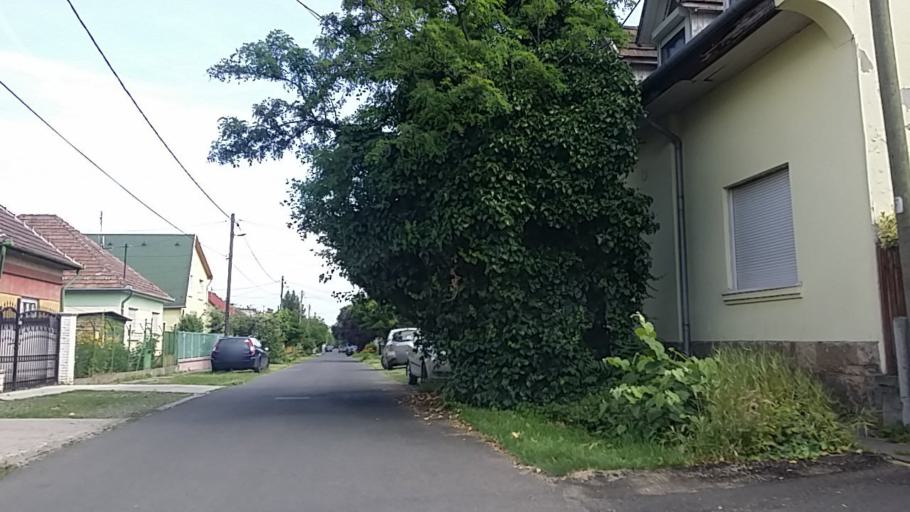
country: HU
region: Budapest
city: Budapest XXI. keruelet
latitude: 47.4133
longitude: 19.0691
